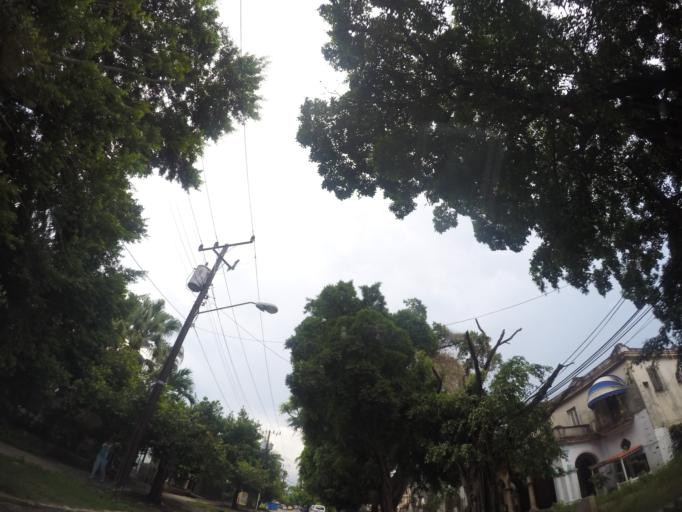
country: CU
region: La Habana
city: Havana
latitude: 23.1234
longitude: -82.4227
